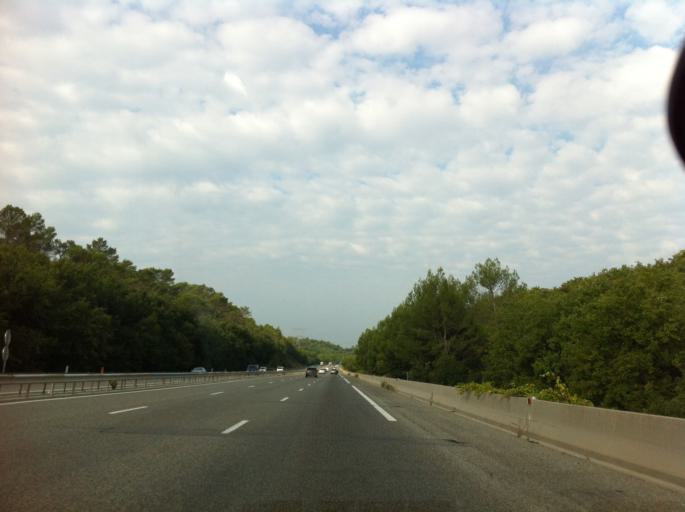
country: FR
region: Provence-Alpes-Cote d'Azur
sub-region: Departement du Var
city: Le Luc
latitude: 43.4017
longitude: 6.2677
